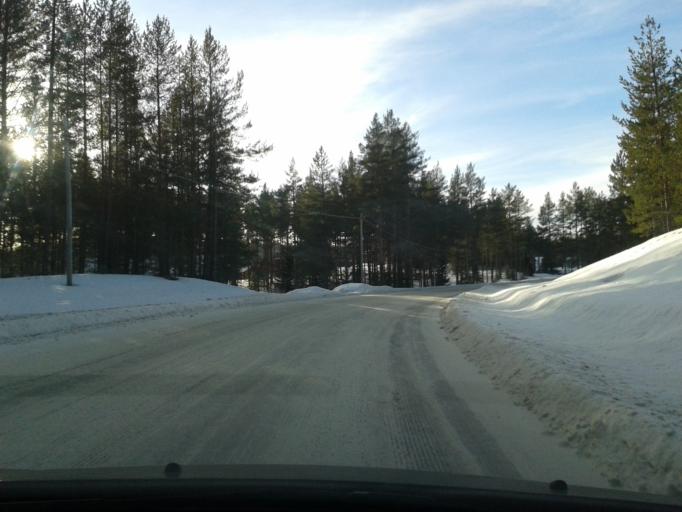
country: SE
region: Vaesternorrland
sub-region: OErnskoeldsviks Kommun
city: Bredbyn
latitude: 63.6736
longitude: 17.8051
